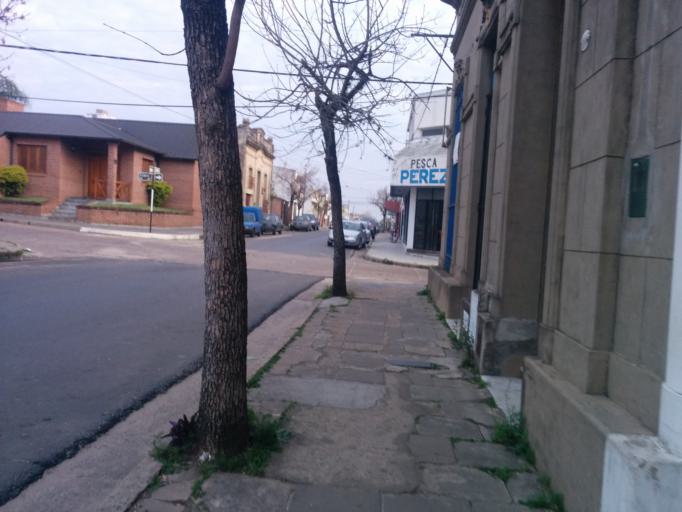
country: AR
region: Entre Rios
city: Concordia
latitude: -31.3898
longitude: -58.0204
